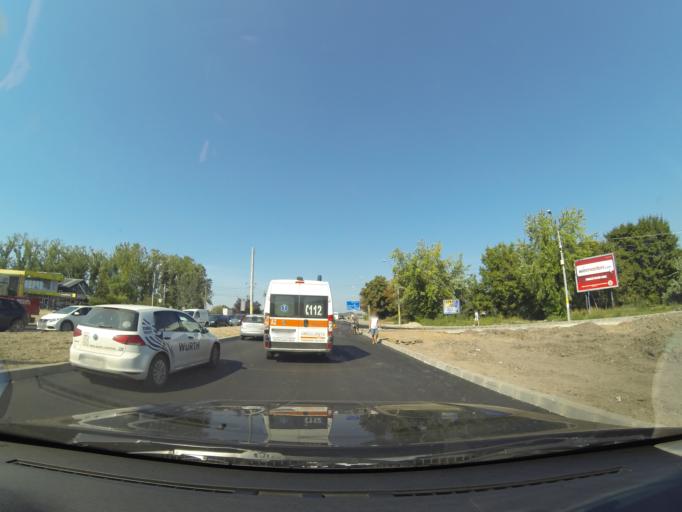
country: RO
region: Arges
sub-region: Comuna Albestii de Arges
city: Pitesti
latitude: 44.8649
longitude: 24.8799
